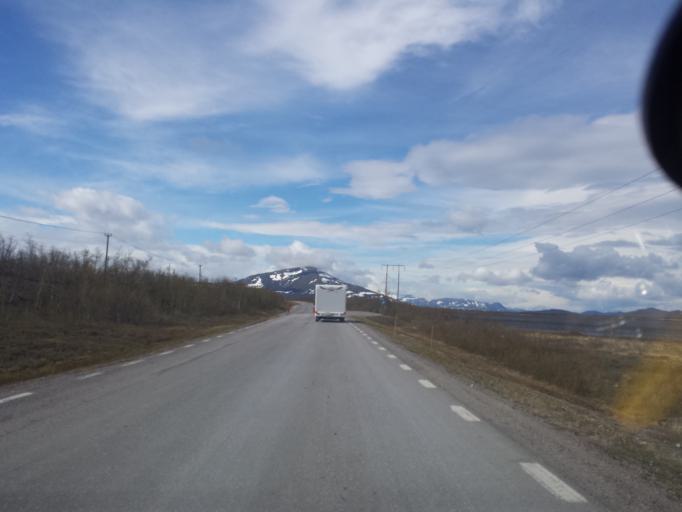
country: SE
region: Norrbotten
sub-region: Kiruna Kommun
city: Kiruna
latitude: 68.1112
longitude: 19.8343
